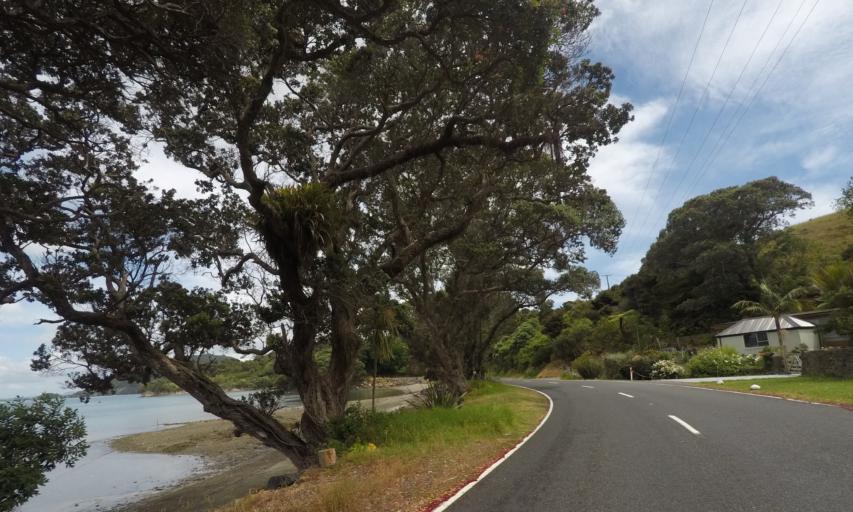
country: NZ
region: Northland
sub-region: Whangarei
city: Ruakaka
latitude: -35.8348
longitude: 174.5331
